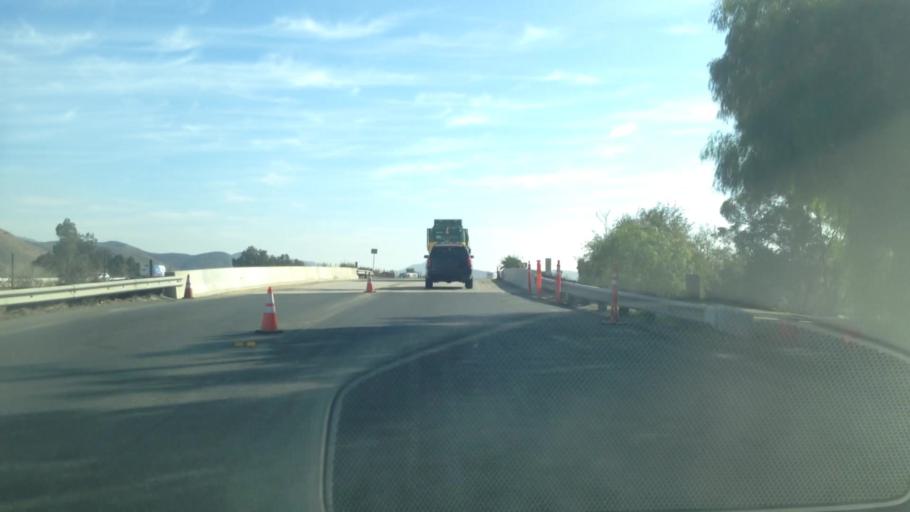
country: US
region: California
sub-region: Riverside County
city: Lake Elsinore
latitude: 33.7409
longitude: -117.4330
